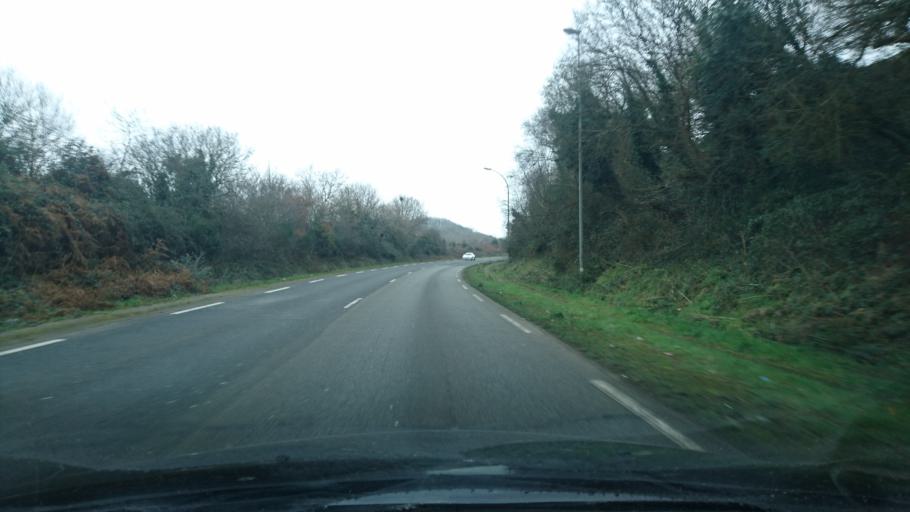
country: FR
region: Brittany
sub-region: Departement du Finistere
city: Guilers
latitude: 48.3902
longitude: -4.5354
